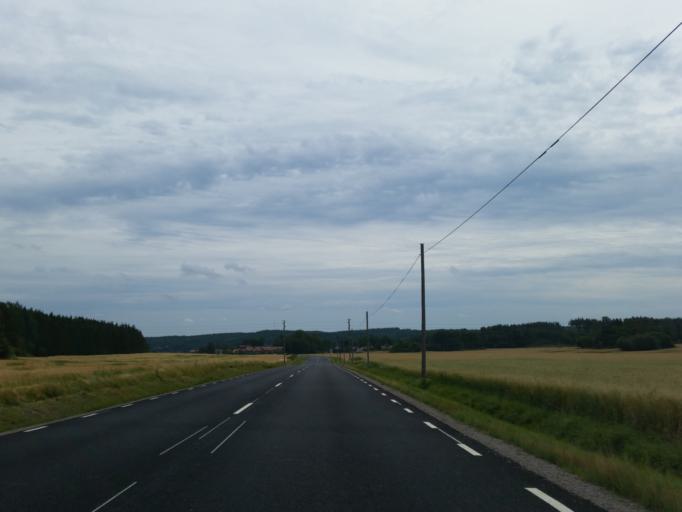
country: SE
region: Soedermanland
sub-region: Strangnas Kommun
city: Mariefred
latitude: 59.2598
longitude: 17.1700
